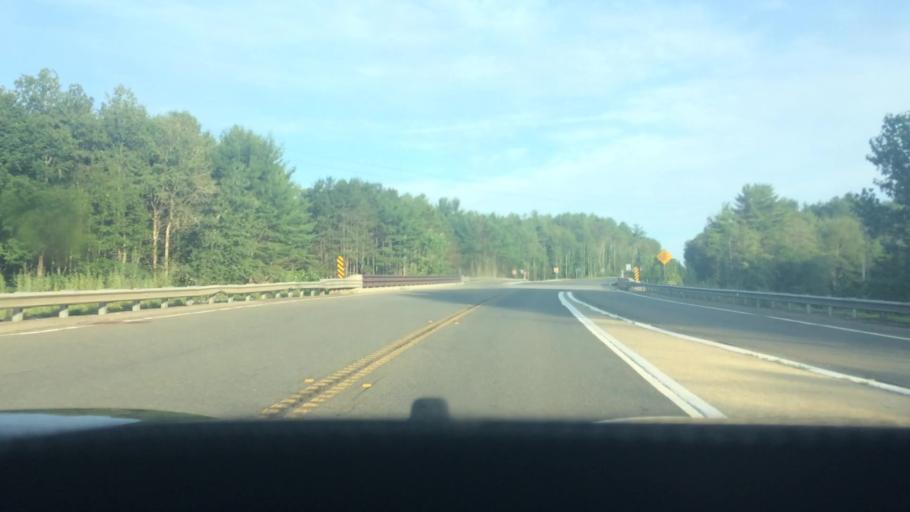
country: US
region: Massachusetts
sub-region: Franklin County
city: Orange
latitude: 42.5582
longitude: -72.3005
